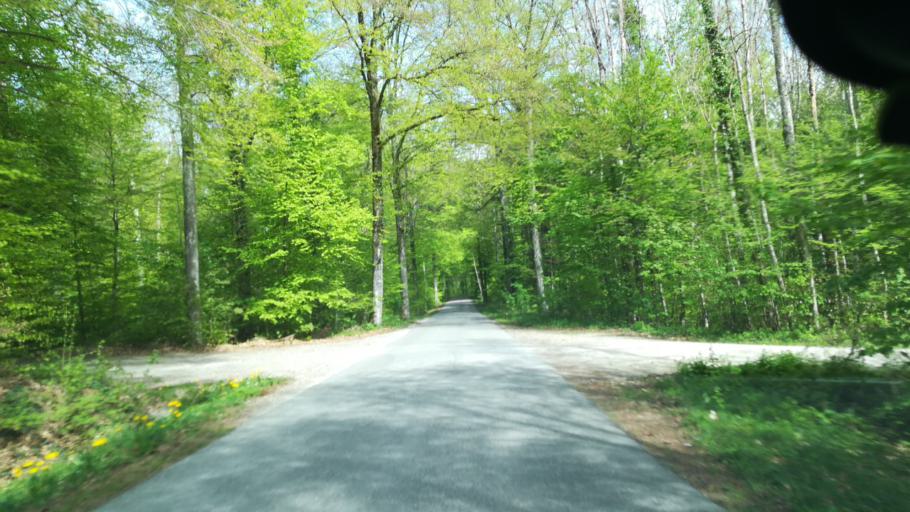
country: CH
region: Thurgau
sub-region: Kreuzlingen District
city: Ermatingen
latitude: 47.6459
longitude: 9.0787
